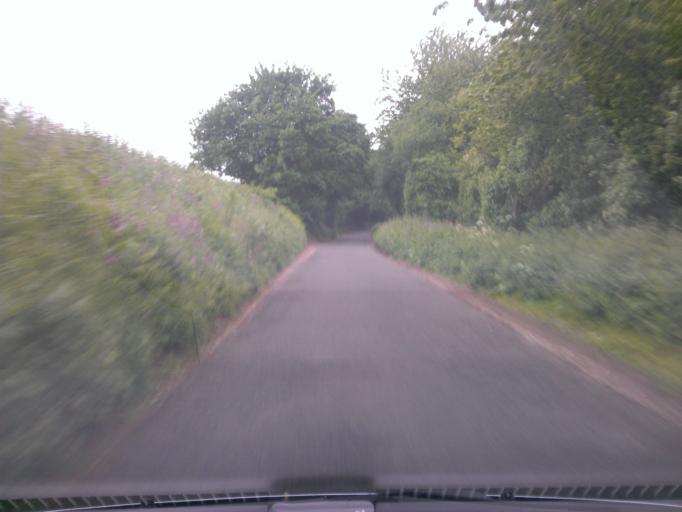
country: GB
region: England
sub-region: Essex
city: Layer de la Haye
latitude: 51.8471
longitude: 0.8106
